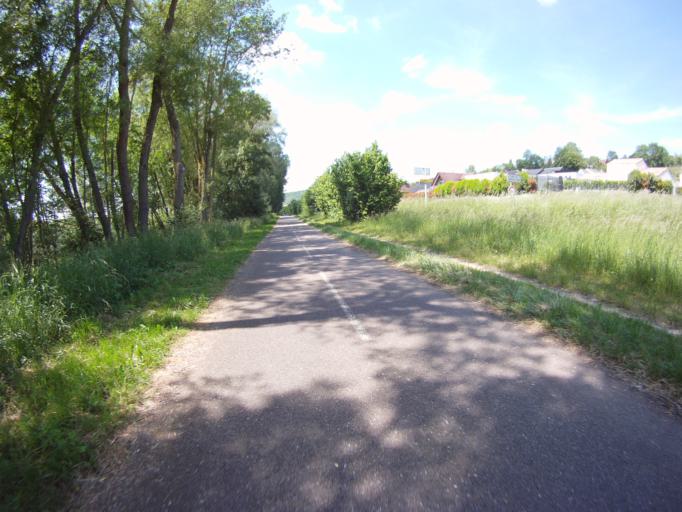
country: FR
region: Lorraine
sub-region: Departement de Meurthe-et-Moselle
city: Lay-Saint-Christophe
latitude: 48.7445
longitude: 6.2108
